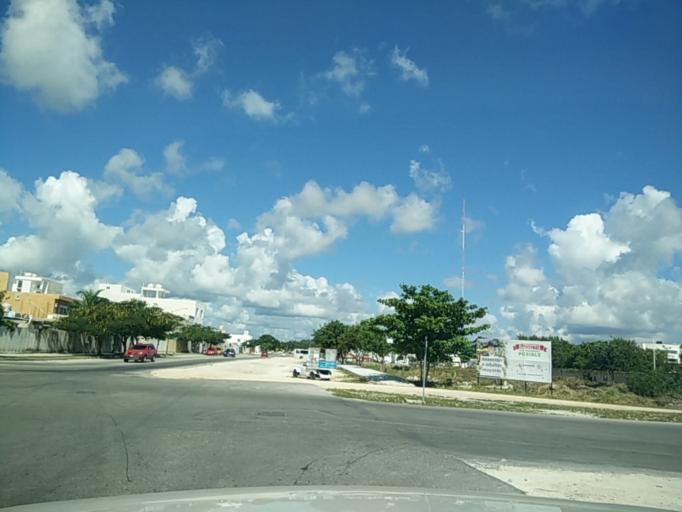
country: MX
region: Quintana Roo
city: Playa del Carmen
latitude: 20.6641
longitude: -87.0646
